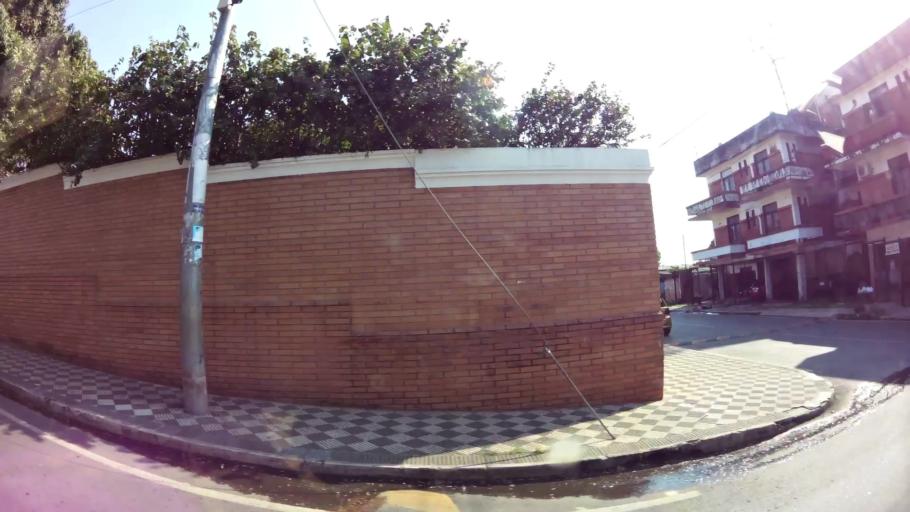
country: PY
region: Asuncion
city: Asuncion
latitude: -25.3063
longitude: -57.6244
